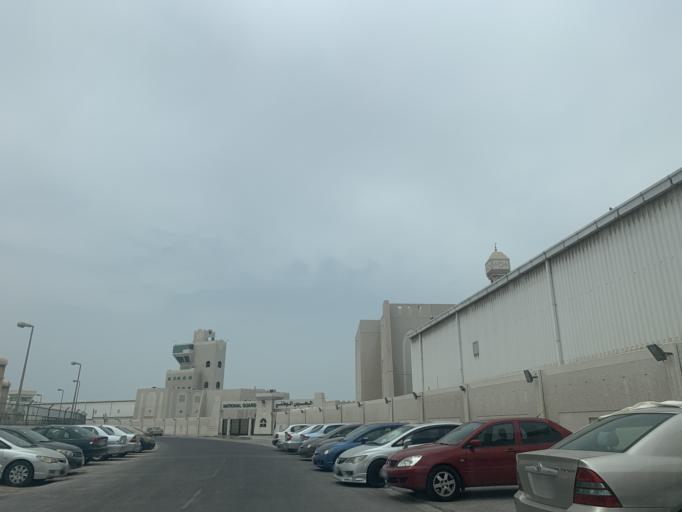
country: BH
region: Muharraq
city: Al Hadd
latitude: 26.2178
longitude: 50.6527
